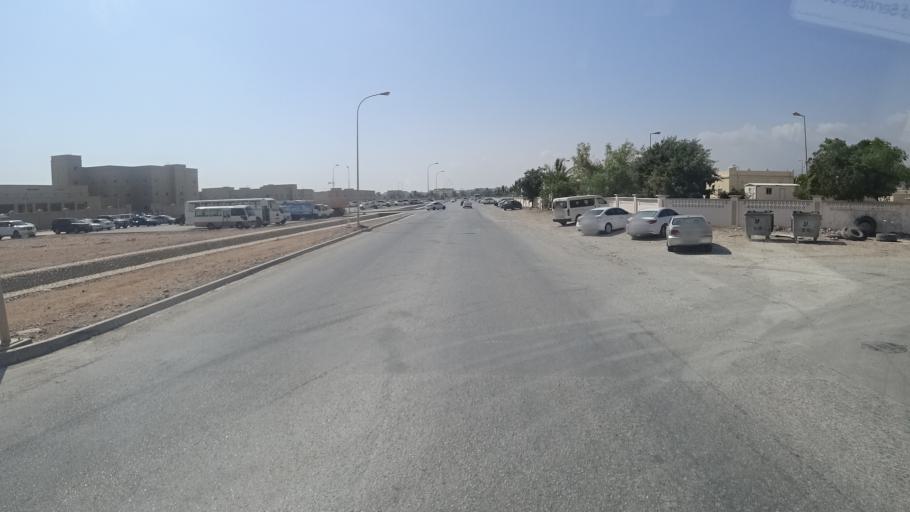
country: OM
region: Zufar
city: Salalah
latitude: 17.0182
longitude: 54.0403
